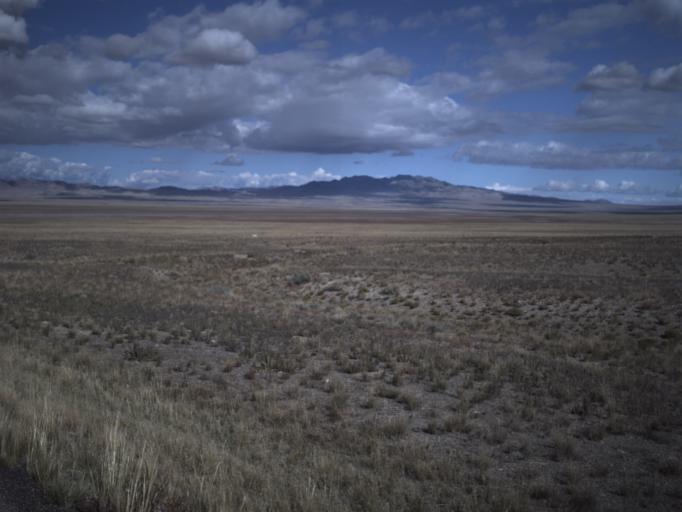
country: US
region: Utah
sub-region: Beaver County
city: Milford
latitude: 38.5141
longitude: -113.6326
